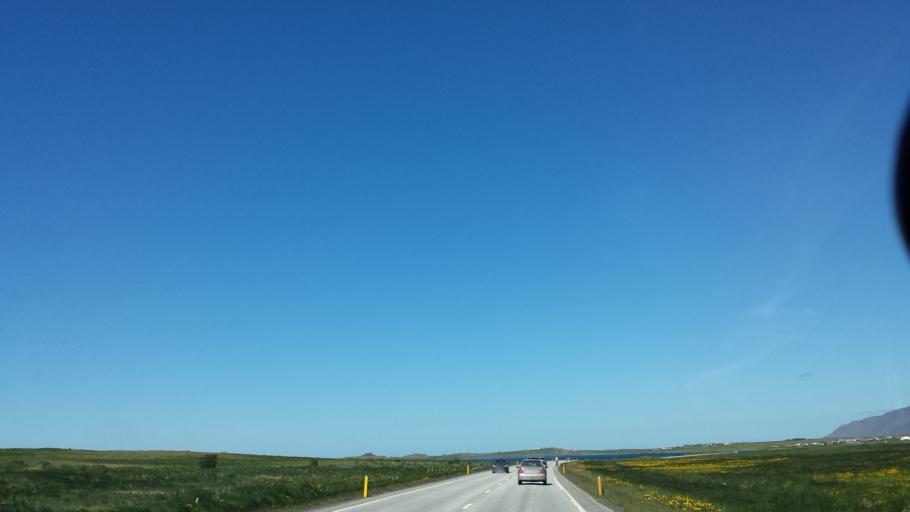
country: IS
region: Capital Region
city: Mosfellsbaer
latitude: 64.2196
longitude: -21.7985
